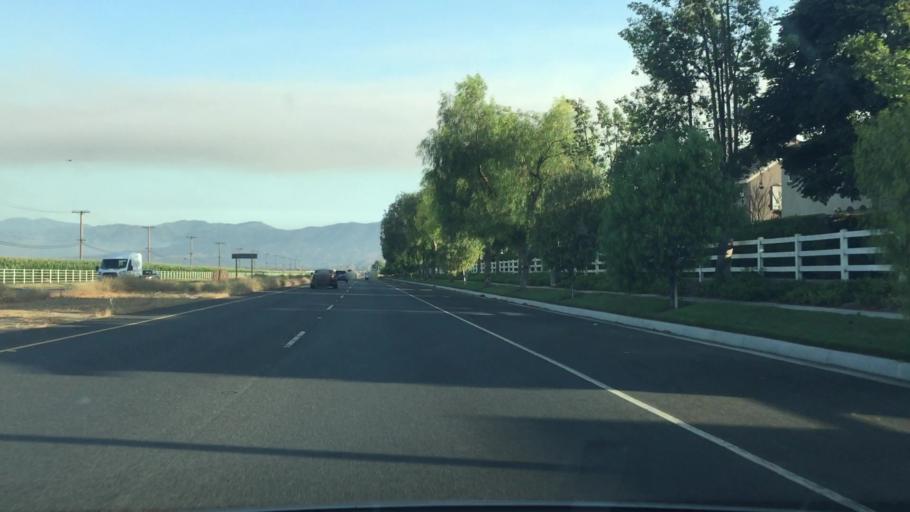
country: US
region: California
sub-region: San Bernardino County
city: Chino
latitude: 33.9896
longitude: -117.6509
